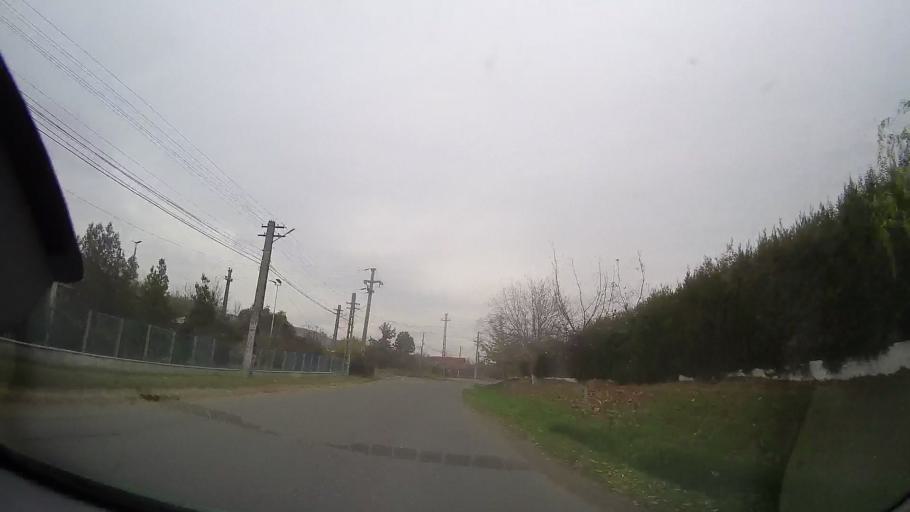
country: RO
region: Prahova
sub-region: Oras Urlati
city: Urlati
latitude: 45.0010
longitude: 26.2276
